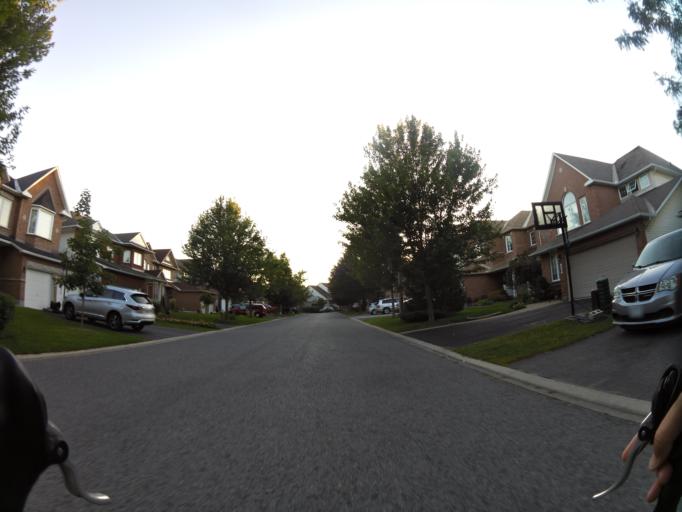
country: CA
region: Ontario
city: Bells Corners
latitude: 45.3500
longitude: -75.9341
